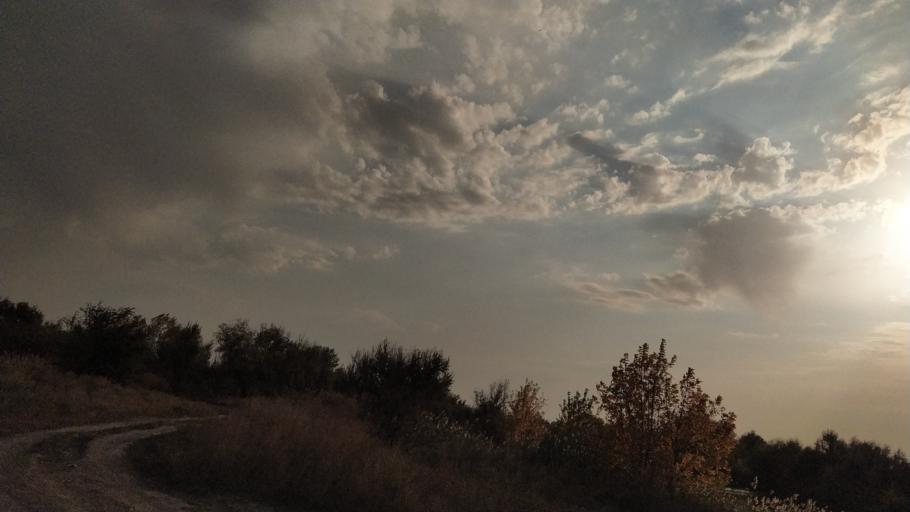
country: RU
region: Rostov
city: Kuleshovka
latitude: 47.1233
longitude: 39.6046
